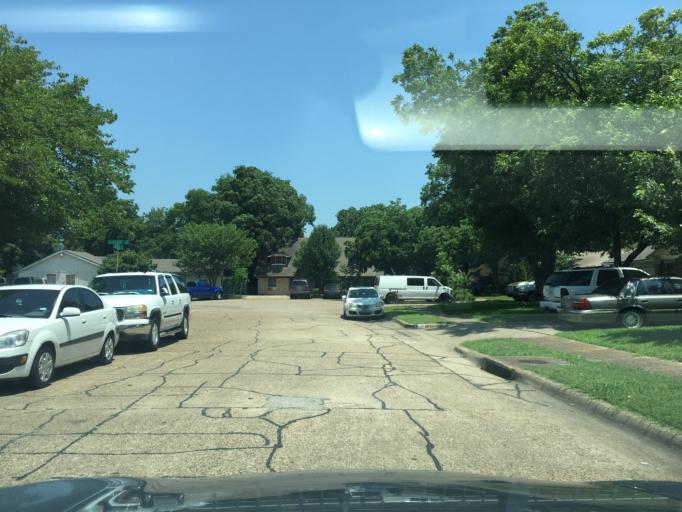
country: US
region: Texas
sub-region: Dallas County
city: Garland
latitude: 32.9151
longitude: -96.6889
